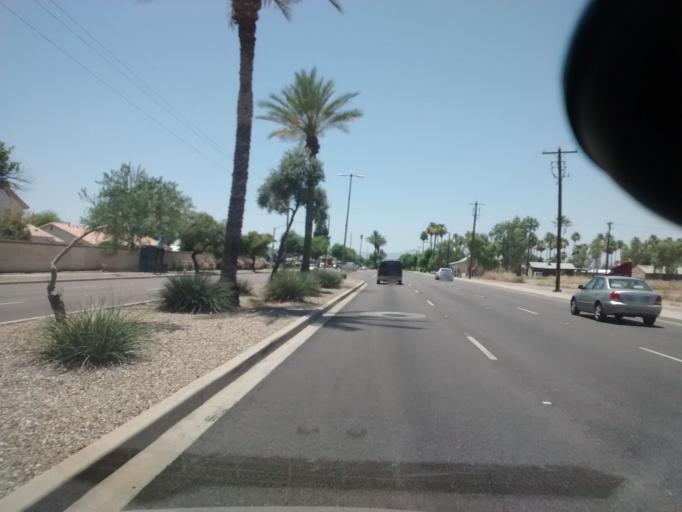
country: US
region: Arizona
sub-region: Maricopa County
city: Glendale
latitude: 33.5379
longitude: -112.2277
